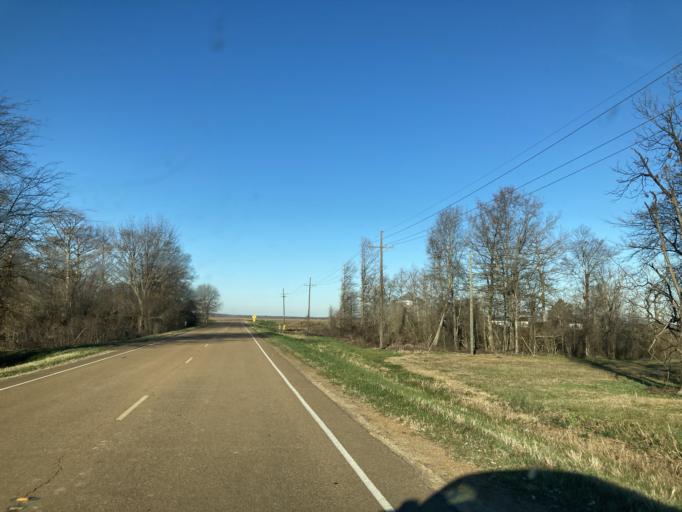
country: US
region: Mississippi
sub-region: Yazoo County
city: Yazoo City
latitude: 32.9303
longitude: -90.5974
